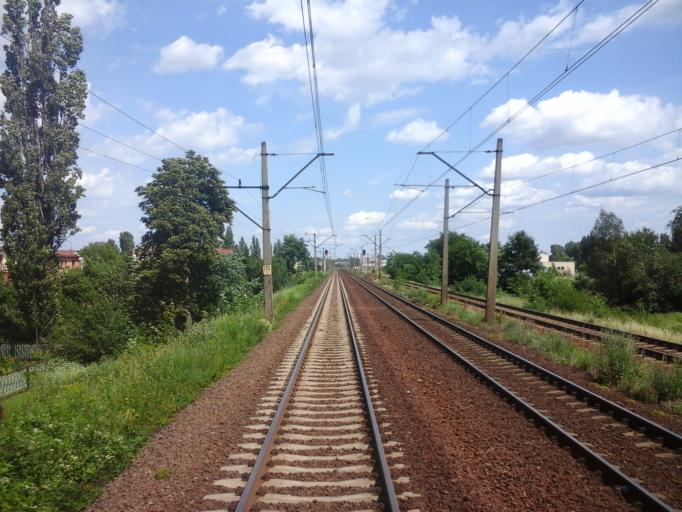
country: PL
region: West Pomeranian Voivodeship
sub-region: Szczecin
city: Szczecin
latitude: 53.3821
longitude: 14.6437
